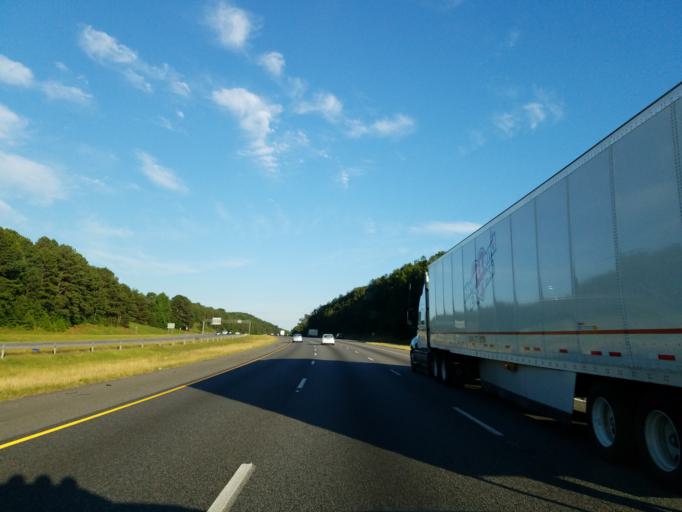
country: US
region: Georgia
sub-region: Bartow County
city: Emerson
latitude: 34.1161
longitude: -84.7377
